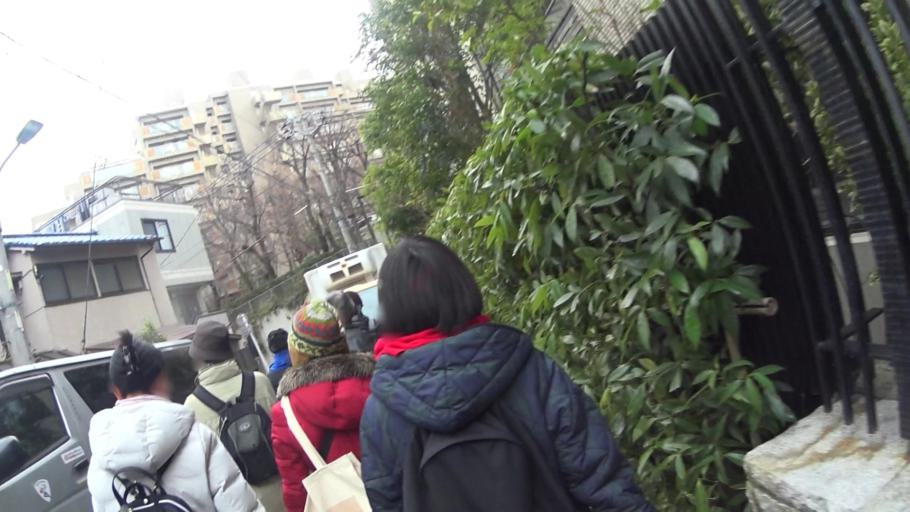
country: JP
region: Kanagawa
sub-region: Kawasaki-shi
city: Kawasaki
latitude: 35.5867
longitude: 139.7244
